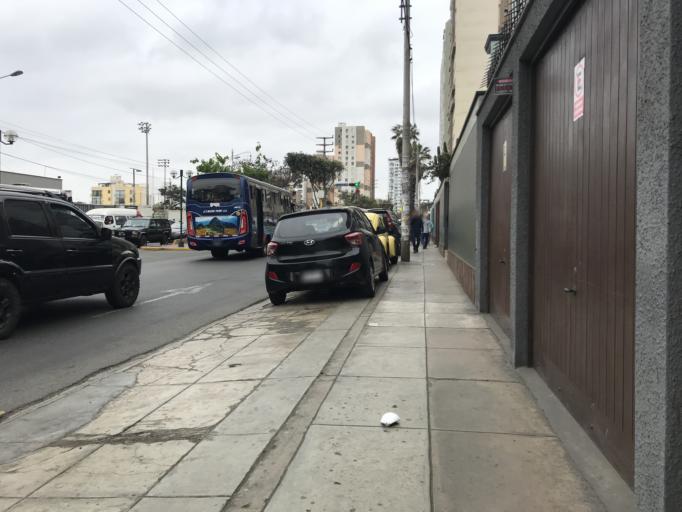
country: PE
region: Callao
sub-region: Callao
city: Callao
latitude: -12.0752
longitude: -77.0780
